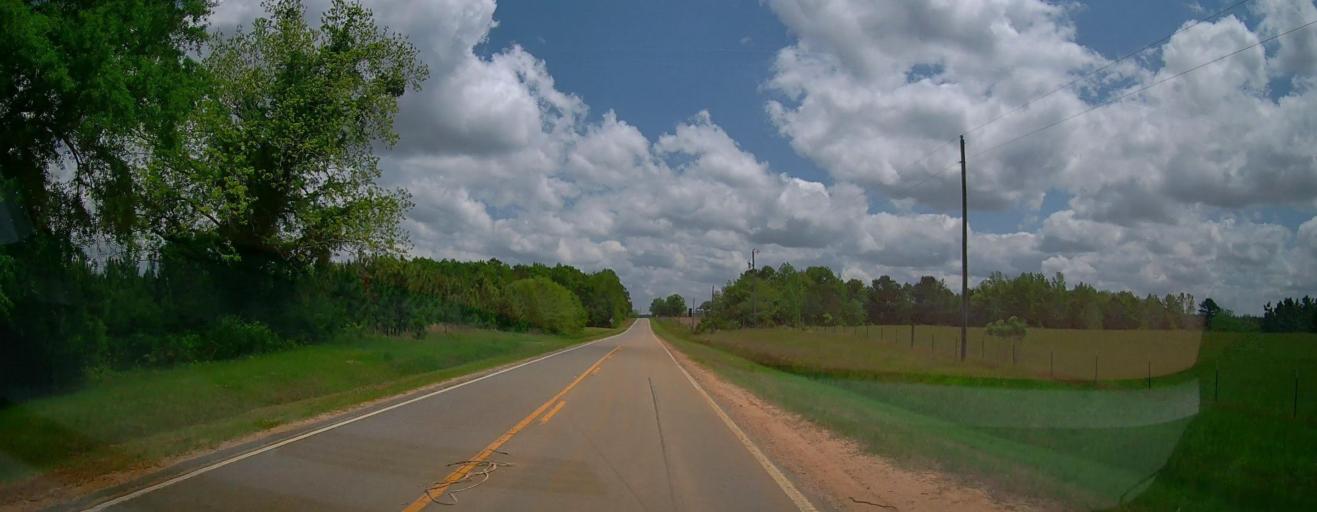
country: US
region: Georgia
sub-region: Dodge County
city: Chester
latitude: 32.5396
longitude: -83.1909
